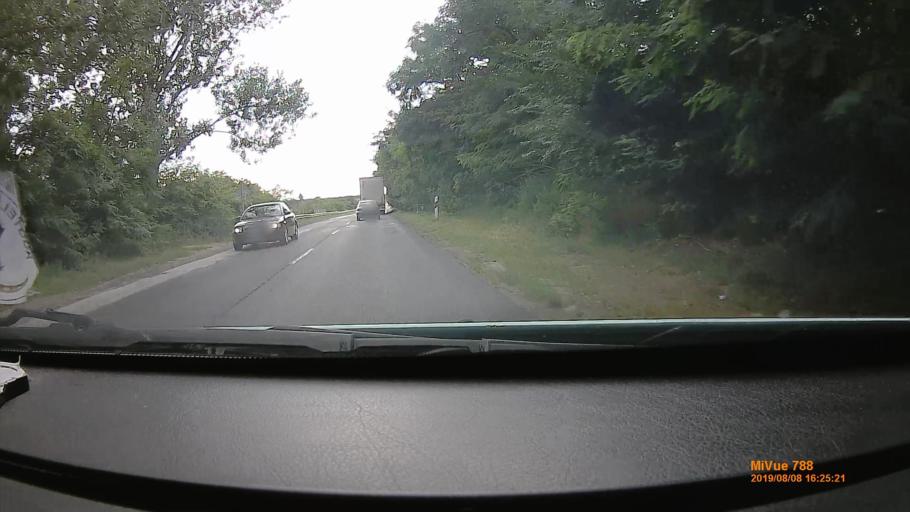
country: HU
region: Szabolcs-Szatmar-Bereg
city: Hodasz
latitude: 47.9691
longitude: 22.2155
